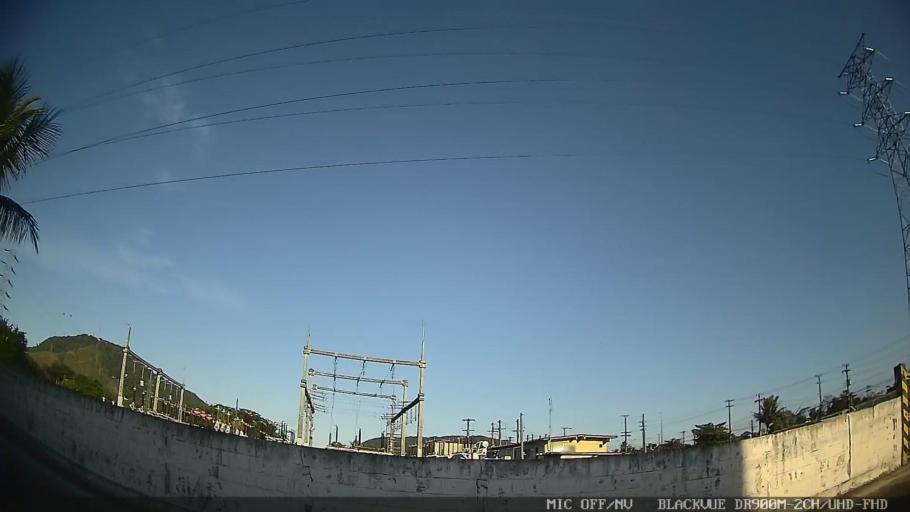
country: BR
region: Sao Paulo
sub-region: Guaruja
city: Guaruja
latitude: -23.9748
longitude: -46.2737
